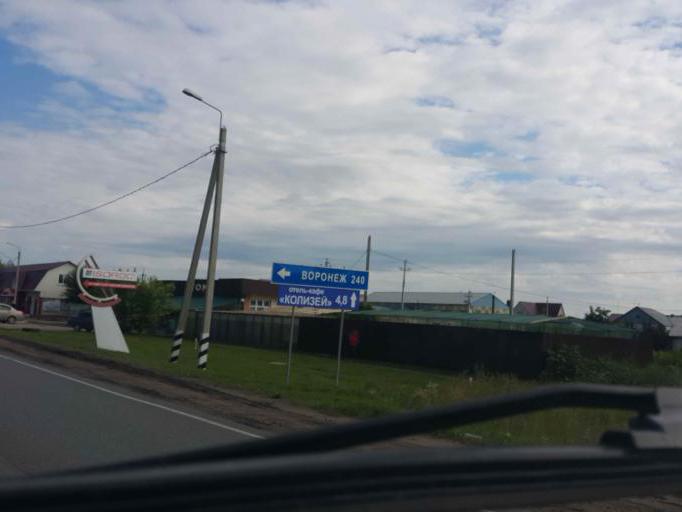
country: RU
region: Tambov
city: Bokino
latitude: 52.6293
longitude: 41.4428
